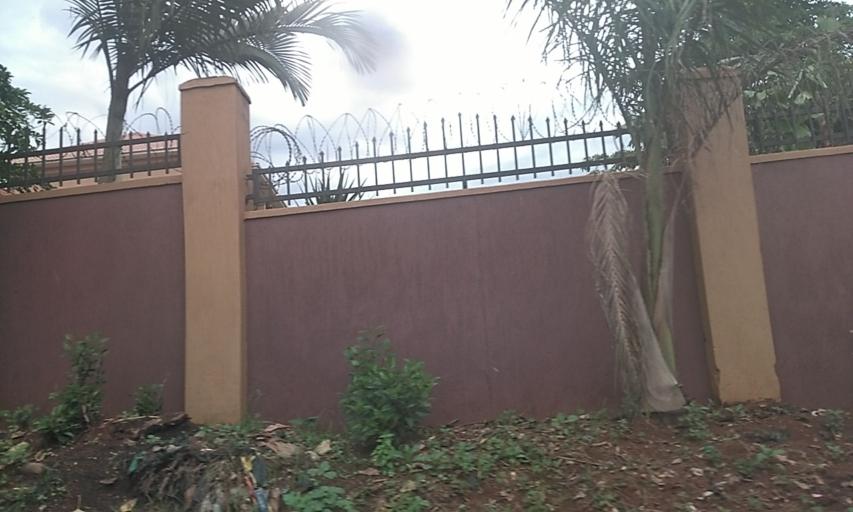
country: UG
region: Central Region
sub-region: Wakiso District
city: Kireka
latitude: 0.3718
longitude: 32.6420
